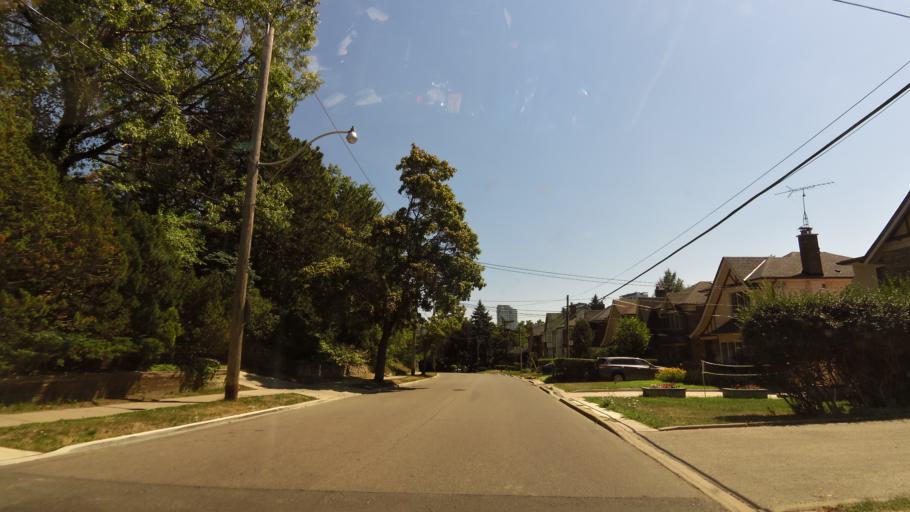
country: CA
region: Ontario
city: Toronto
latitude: 43.6433
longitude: -79.4715
